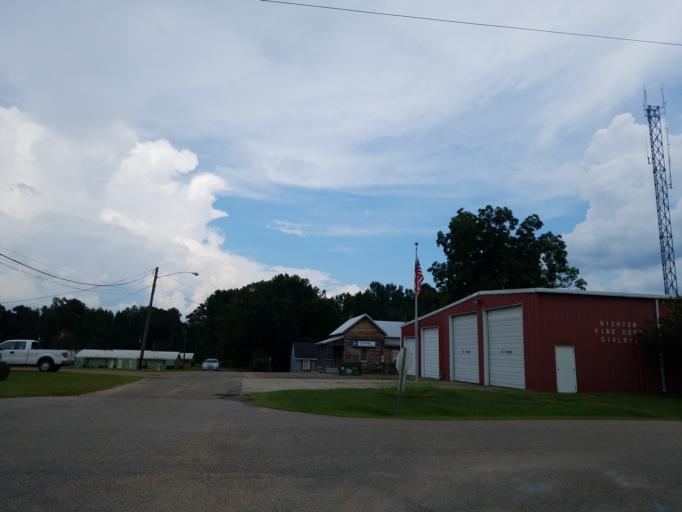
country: US
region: Mississippi
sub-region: Perry County
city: Richton
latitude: 31.3498
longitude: -88.9351
